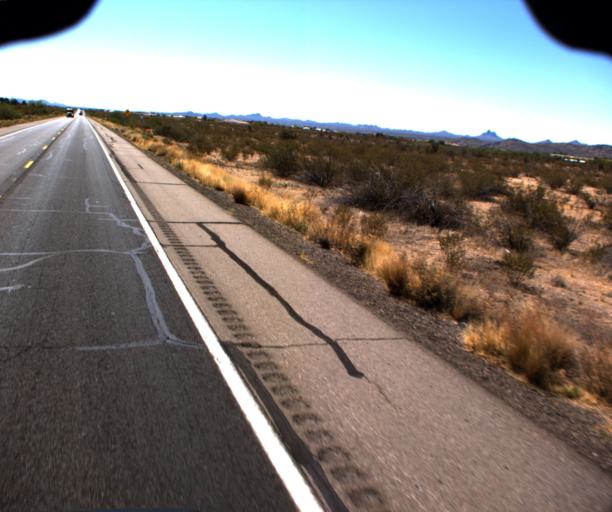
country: US
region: Arizona
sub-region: Yavapai County
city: Congress
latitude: 34.0488
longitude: -112.8434
